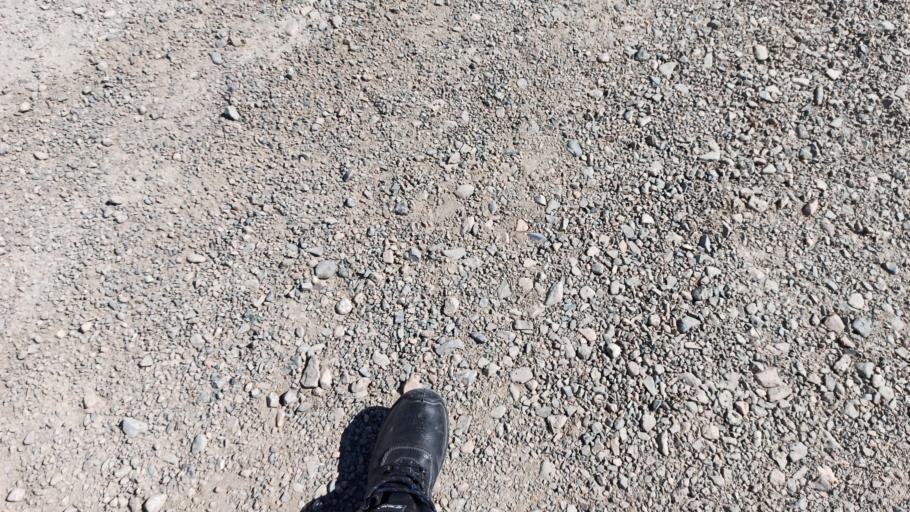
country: KG
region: Chuy
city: Tokmok
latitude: 43.3182
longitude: 75.4594
